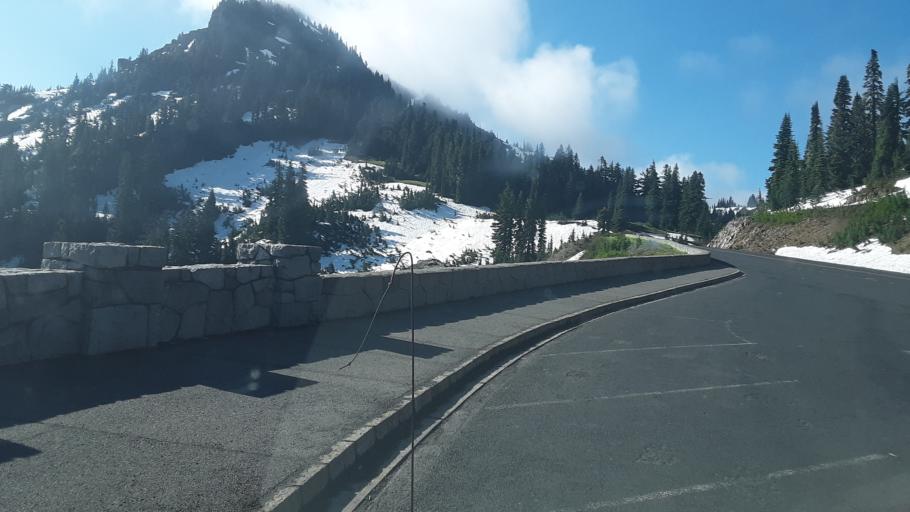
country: US
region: Washington
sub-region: King County
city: Enumclaw
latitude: 46.8743
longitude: -121.5159
